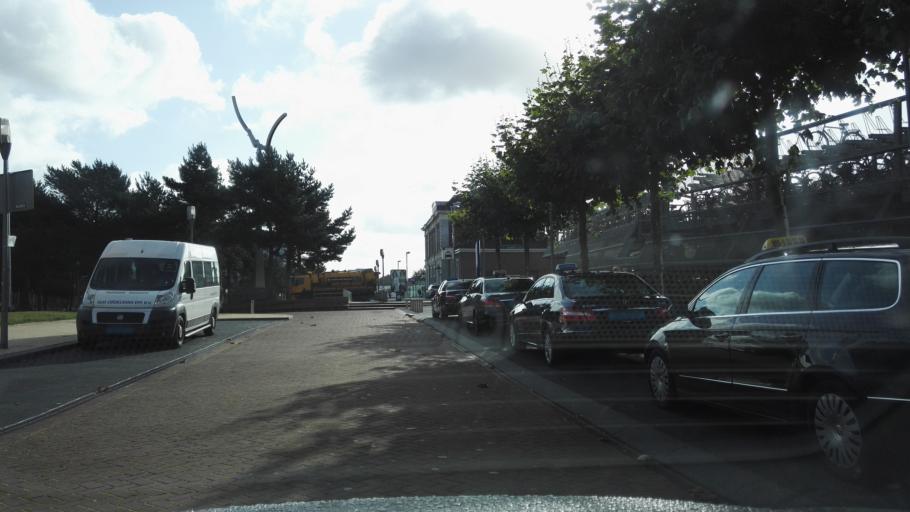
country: NL
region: Gelderland
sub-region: Gemeente Apeldoorn
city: Apeldoorn
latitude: 52.2097
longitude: 5.9671
